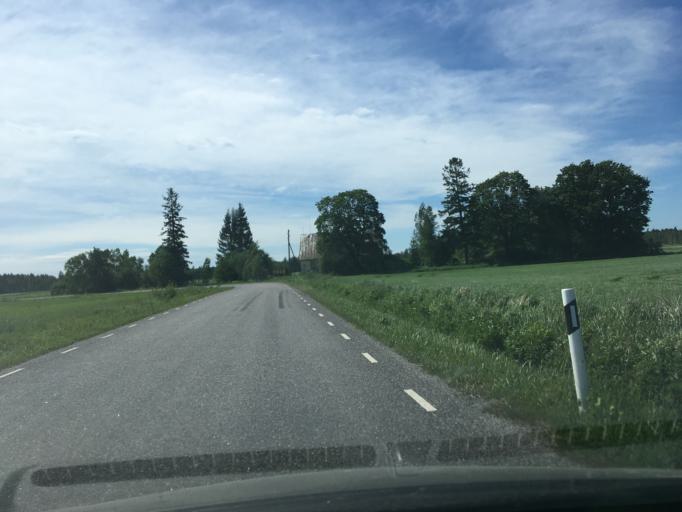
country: EE
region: Paernumaa
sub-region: Audru vald
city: Audru
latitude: 58.4321
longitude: 24.3994
